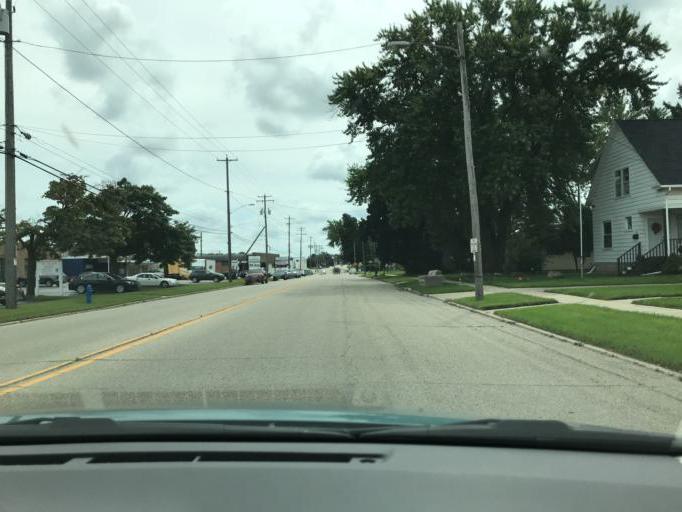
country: US
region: Wisconsin
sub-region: Racine County
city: Burlington
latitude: 42.6709
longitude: -88.2694
